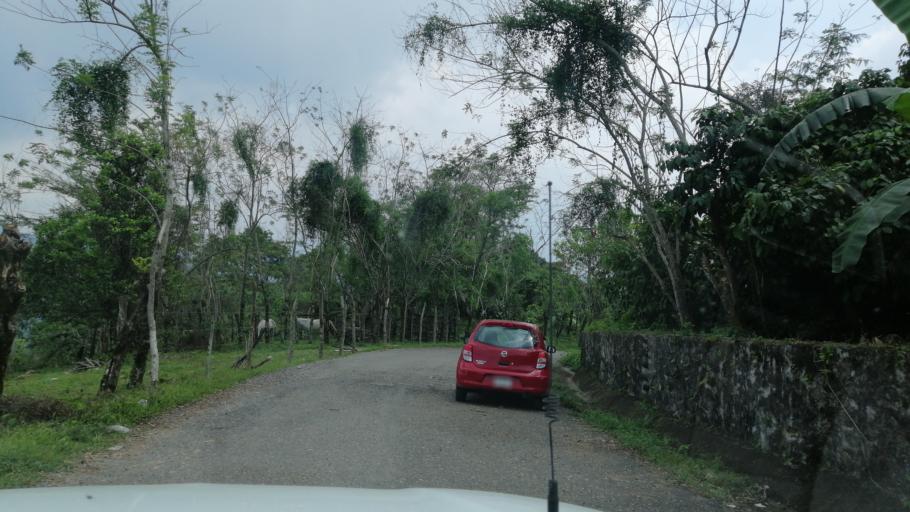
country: MX
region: Chiapas
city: Ostuacan
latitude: 17.3928
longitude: -93.3342
